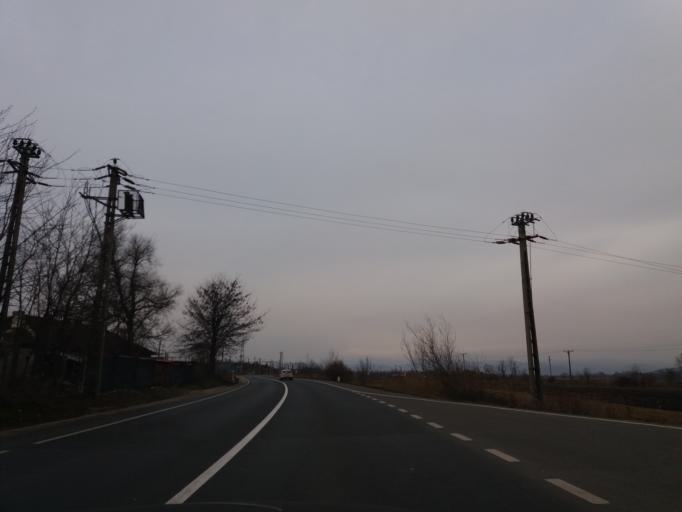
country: RO
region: Hunedoara
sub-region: Comuna Calan
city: Calan
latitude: 45.7594
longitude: 23.0009
